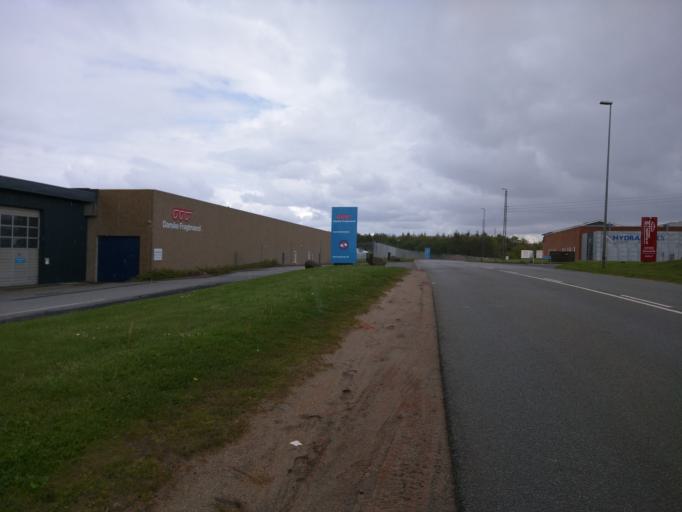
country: DK
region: Central Jutland
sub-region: Viborg Kommune
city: Viborg
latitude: 56.4541
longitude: 9.3726
